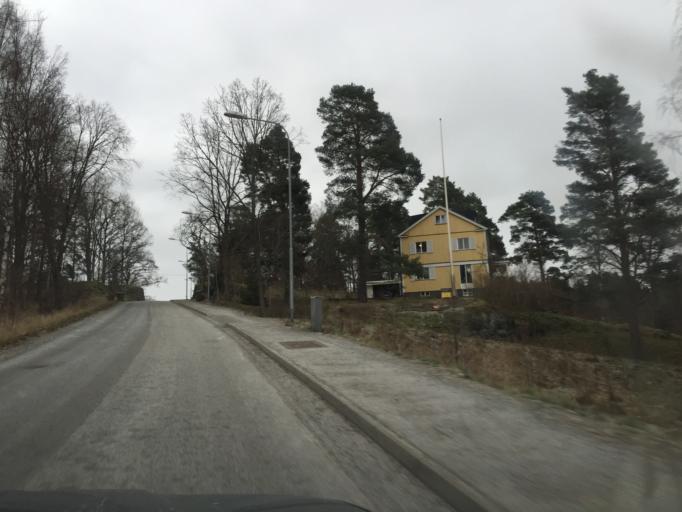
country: SE
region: Stockholm
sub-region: Salems Kommun
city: Ronninge
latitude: 59.1834
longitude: 17.7268
